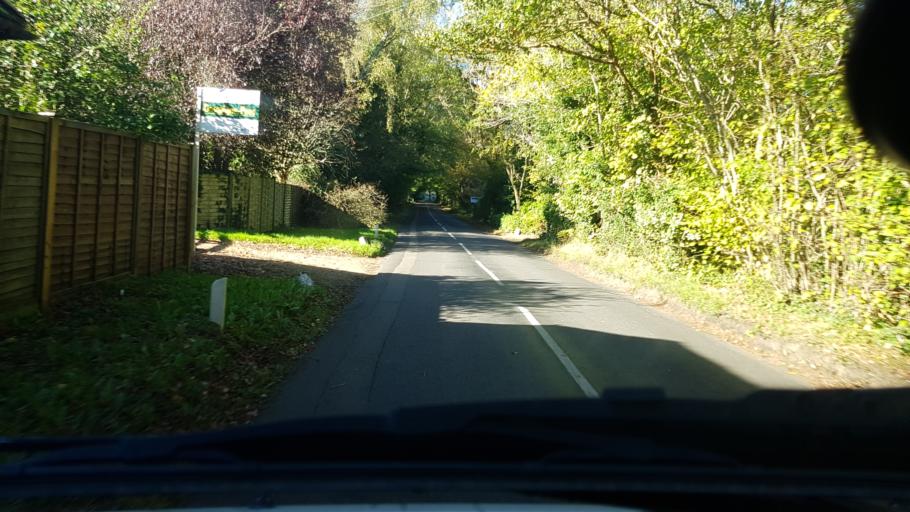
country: GB
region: England
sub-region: Surrey
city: Pirbright
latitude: 51.2692
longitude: -0.6473
